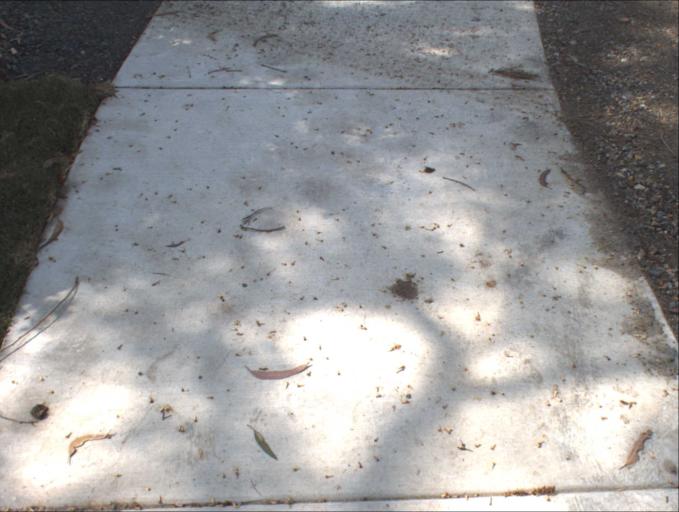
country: AU
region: Queensland
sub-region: Logan
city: Waterford West
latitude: -27.6903
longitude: 153.1611
